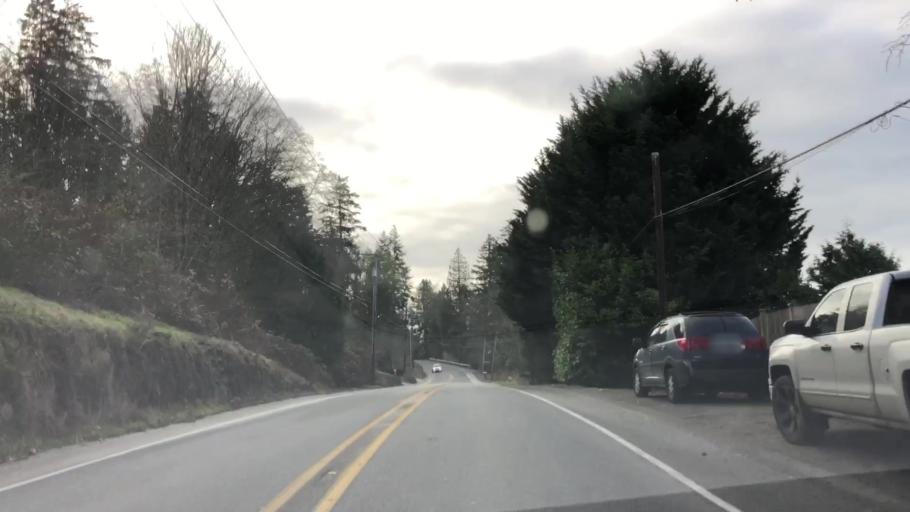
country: US
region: Washington
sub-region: Kitsap County
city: Indianola
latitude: 47.7598
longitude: -122.5509
